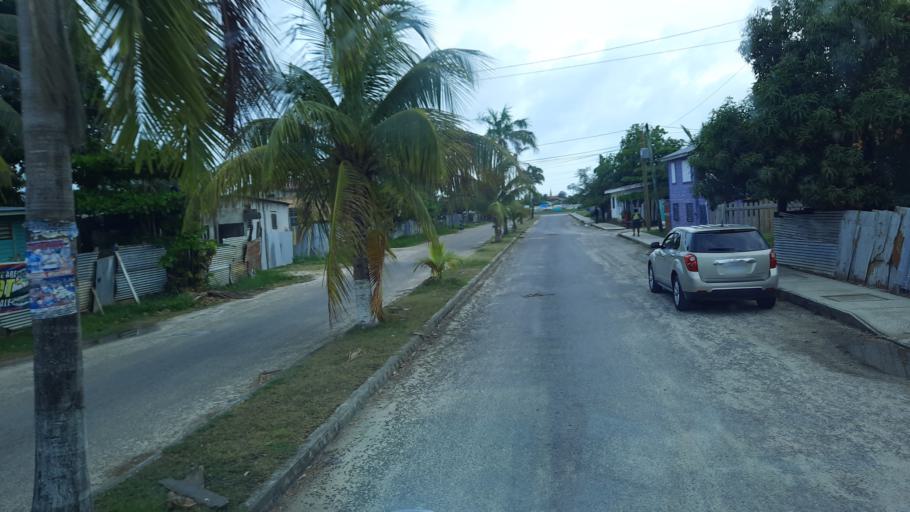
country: BZ
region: Belize
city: Belize City
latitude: 17.5004
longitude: -88.2062
